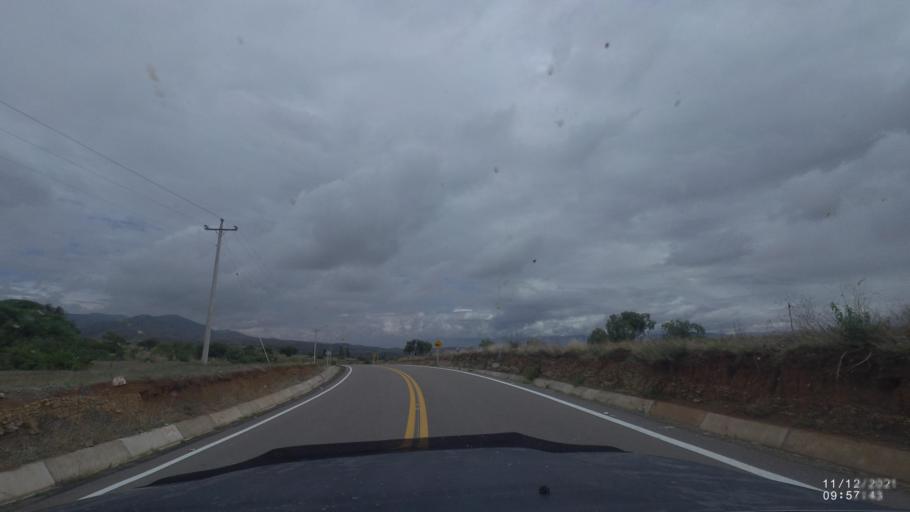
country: BO
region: Cochabamba
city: Cliza
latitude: -17.7571
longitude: -65.9189
